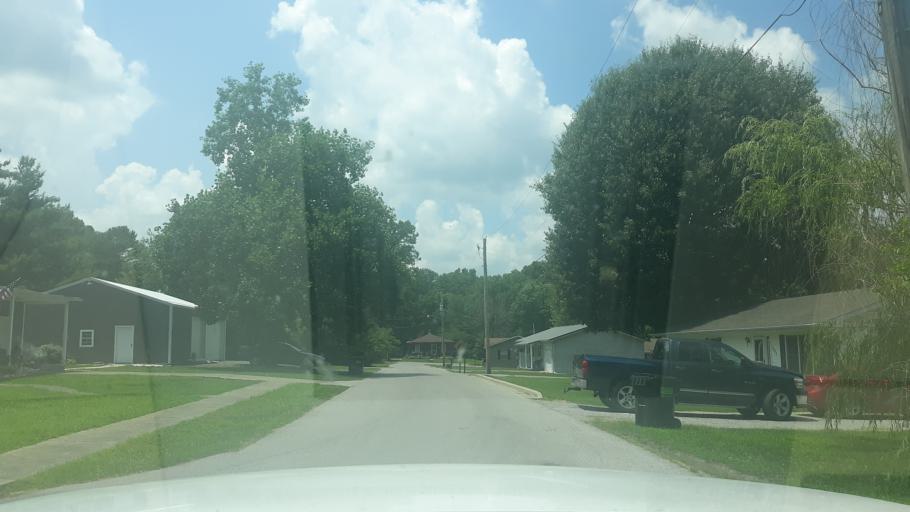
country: US
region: Illinois
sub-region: Saline County
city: Harrisburg
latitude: 37.7241
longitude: -88.5575
